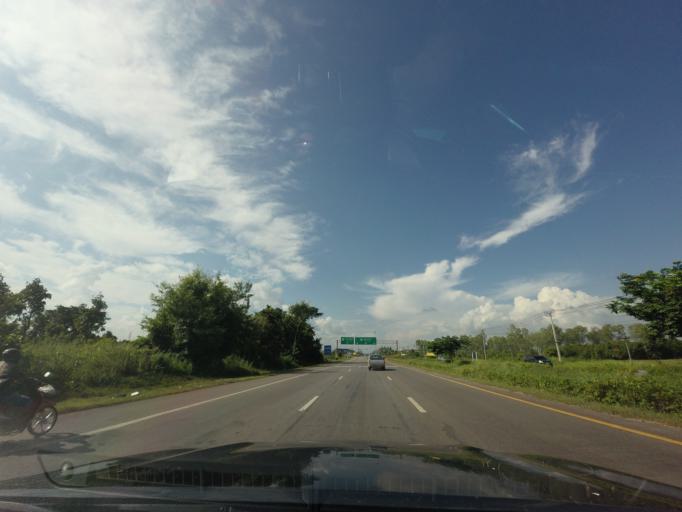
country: TH
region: Nong Khai
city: Nong Khai
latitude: 17.8102
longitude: 102.7596
